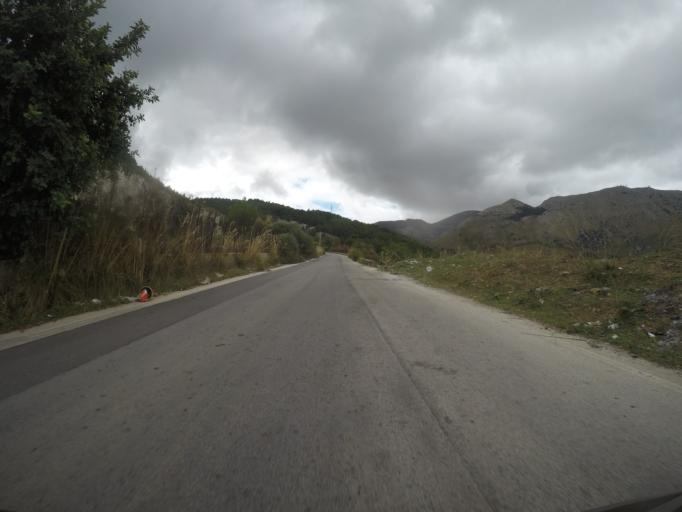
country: IT
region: Sicily
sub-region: Palermo
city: Montelepre
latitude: 38.1179
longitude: 13.1731
